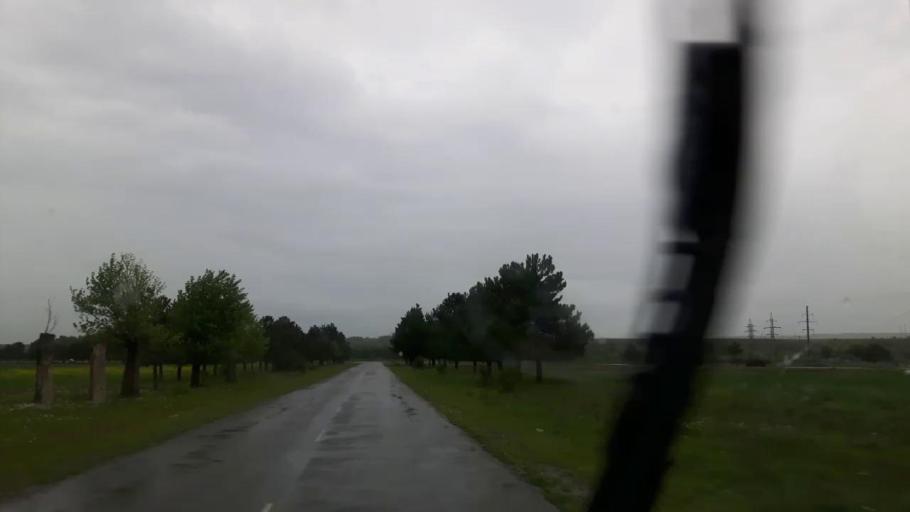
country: GE
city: Agara
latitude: 42.0189
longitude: 43.9067
